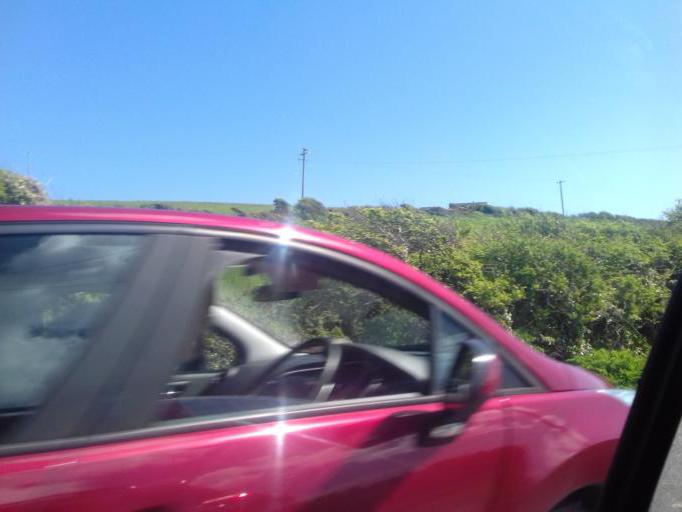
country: IE
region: Munster
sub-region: Waterford
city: Dunmore East
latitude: 52.1744
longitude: -6.8962
